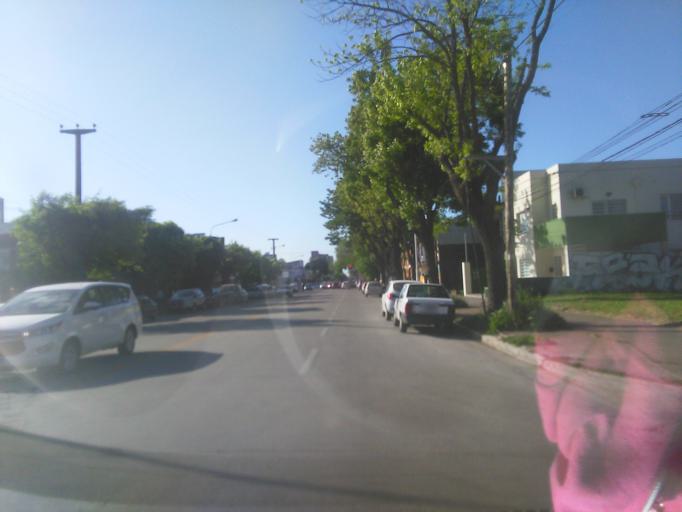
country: AR
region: Buenos Aires
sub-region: Partido de Tandil
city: Tandil
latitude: -37.3326
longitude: -59.1256
